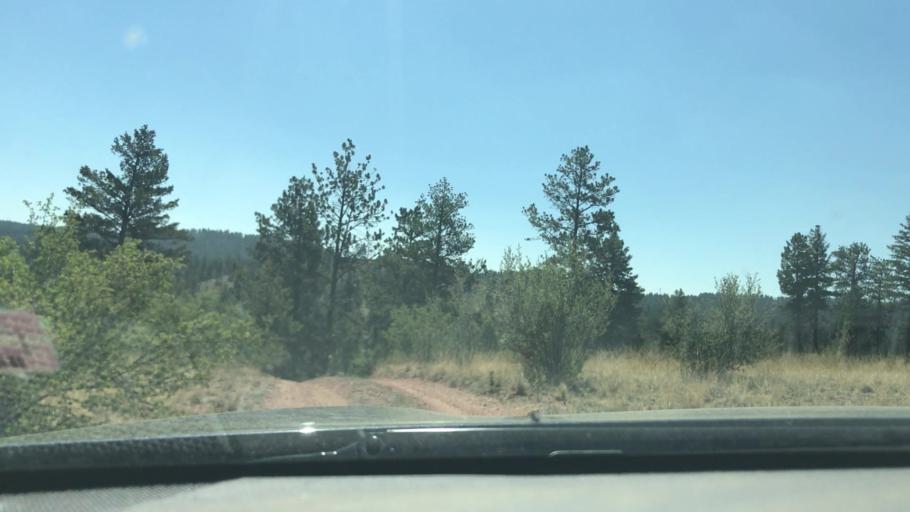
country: US
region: Colorado
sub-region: Teller County
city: Woodland Park
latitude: 38.9979
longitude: -105.3443
